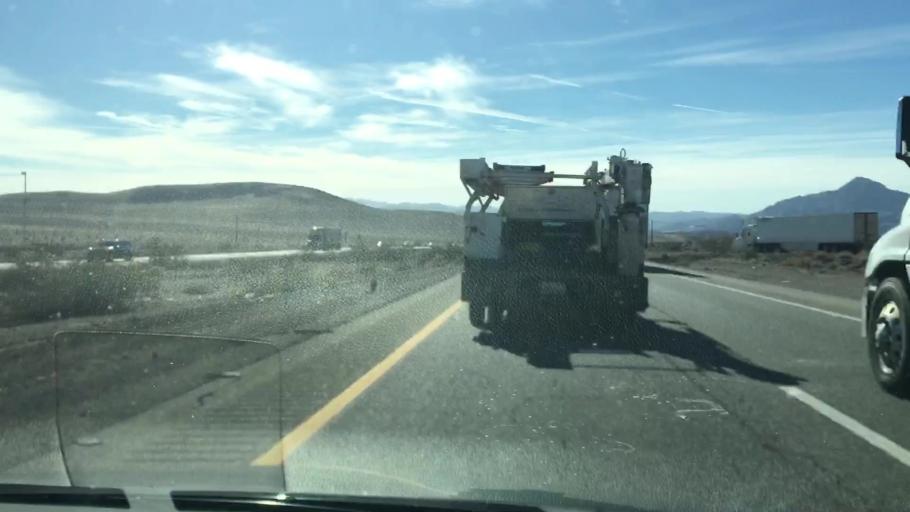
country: US
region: California
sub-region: San Bernardino County
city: Fort Irwin
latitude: 35.1336
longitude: -116.2120
